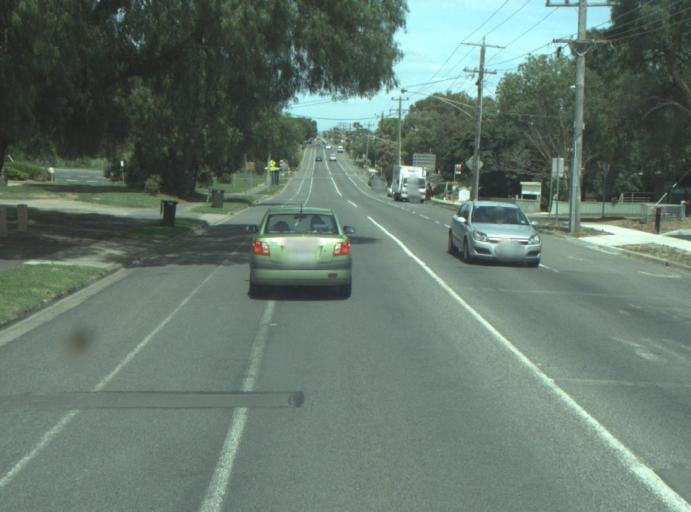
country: AU
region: Victoria
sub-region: Greater Geelong
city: Lara
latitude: -38.0232
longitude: 144.3963
